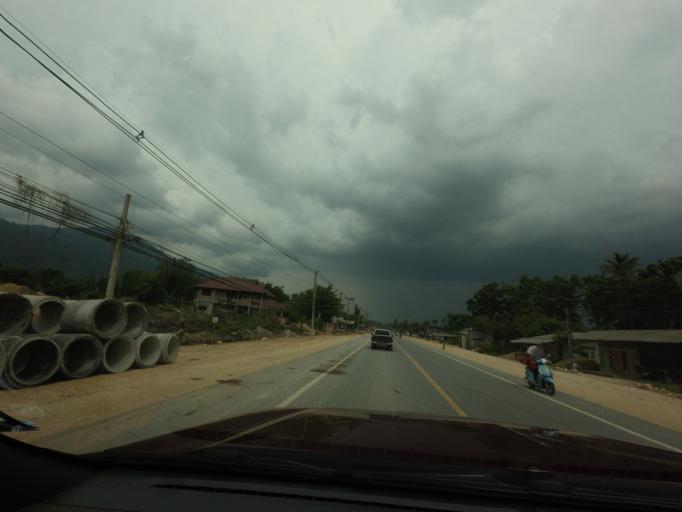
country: TH
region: Yala
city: Krong Pi Nang
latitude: 6.4409
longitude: 101.2777
